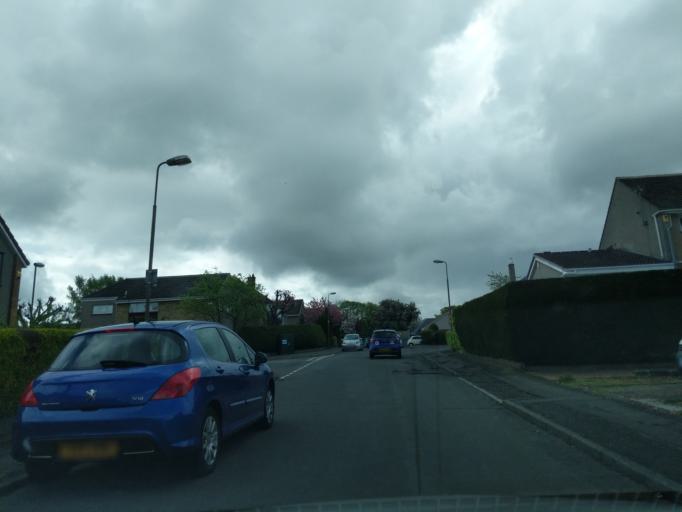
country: GB
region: Scotland
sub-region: Edinburgh
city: Currie
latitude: 55.9004
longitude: -3.2993
